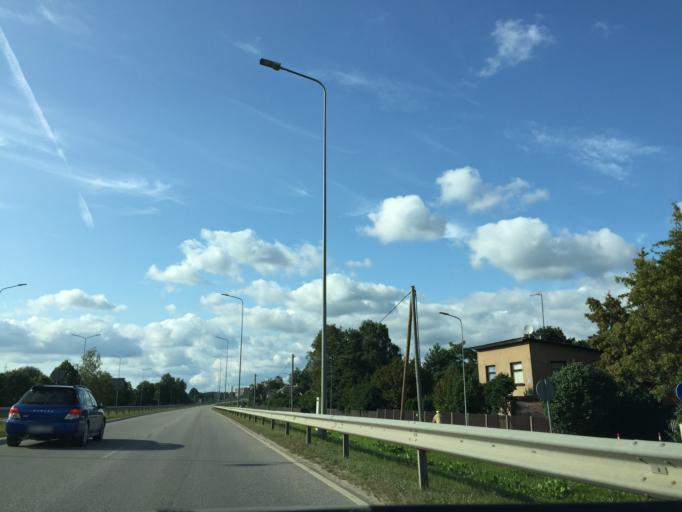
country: LV
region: Ogre
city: Ogre
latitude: 56.8054
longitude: 24.6091
